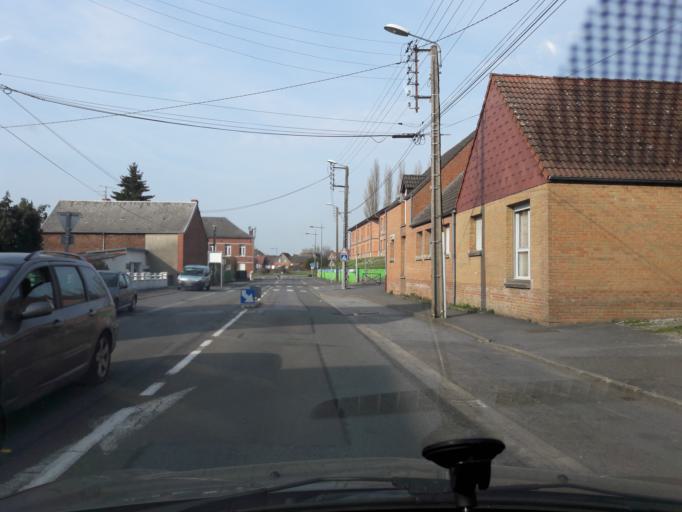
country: FR
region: Nord-Pas-de-Calais
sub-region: Departement du Nord
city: Rousies
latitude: 50.2737
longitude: 4.0064
